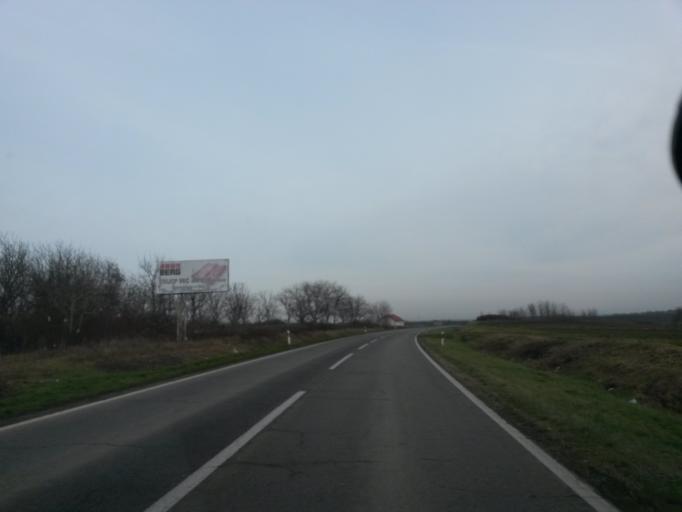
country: HR
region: Vukovarsko-Srijemska
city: Nustar
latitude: 45.3368
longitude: 18.8584
